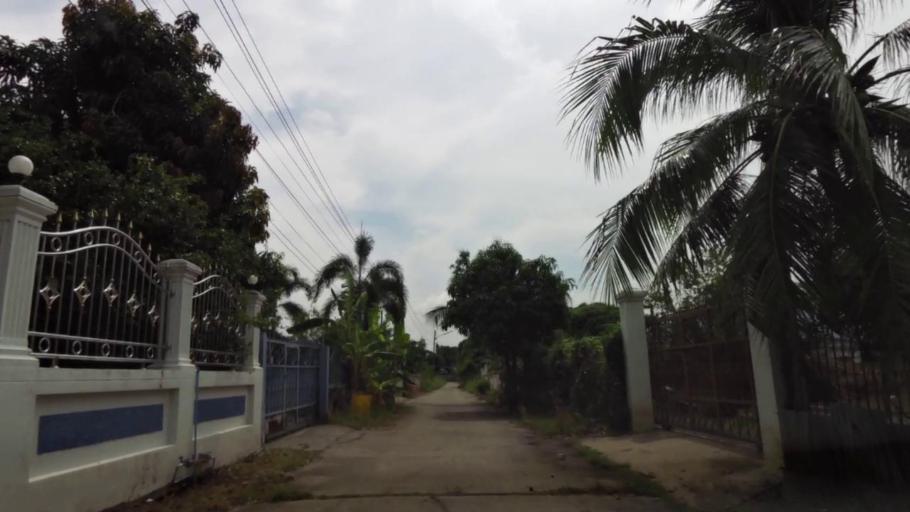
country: TH
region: Lop Buri
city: Ban Mi
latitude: 15.0470
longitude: 100.5694
